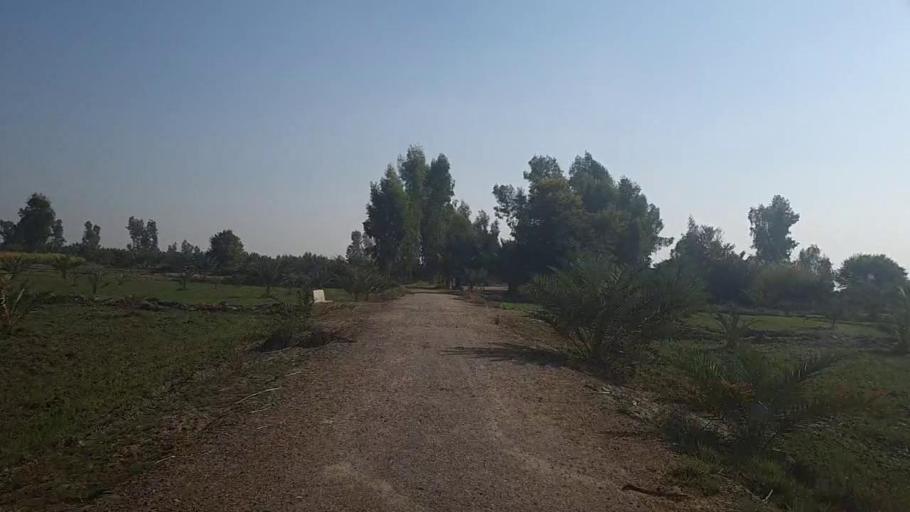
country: PK
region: Sindh
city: Kot Diji
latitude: 27.4331
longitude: 68.7336
